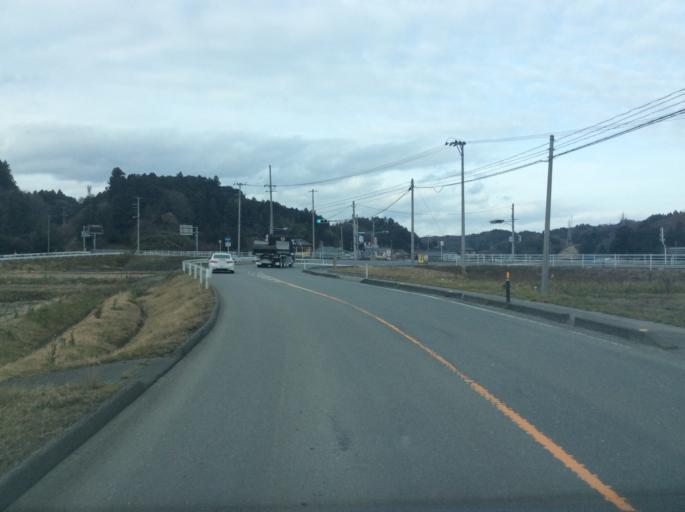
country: JP
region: Fukushima
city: Iwaki
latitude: 37.1204
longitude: 140.9522
